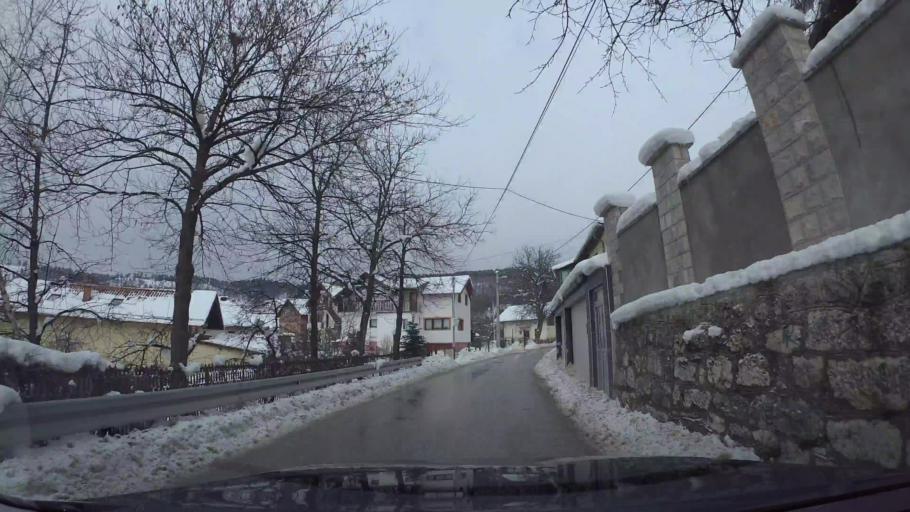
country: BA
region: Federation of Bosnia and Herzegovina
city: Kobilja Glava
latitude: 43.8713
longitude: 18.4414
